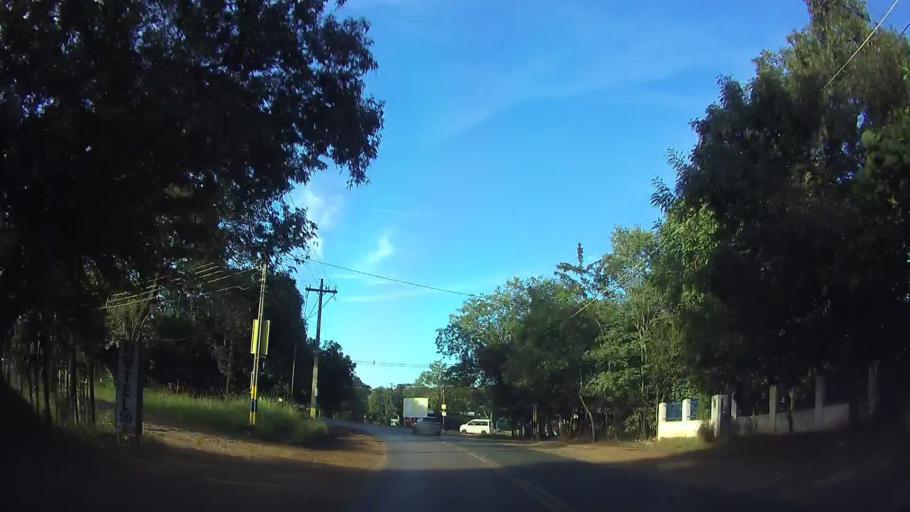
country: PY
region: Central
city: Limpio
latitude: -25.2411
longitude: -57.4751
